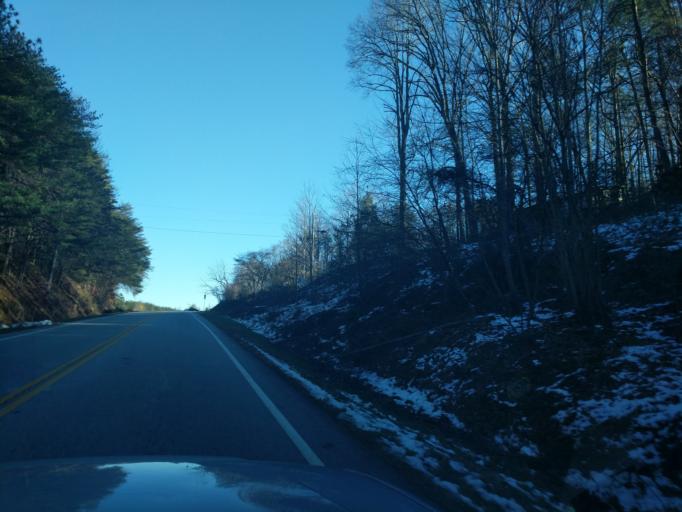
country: US
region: Georgia
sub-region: Rabun County
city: Clayton
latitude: 34.8342
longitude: -83.3279
